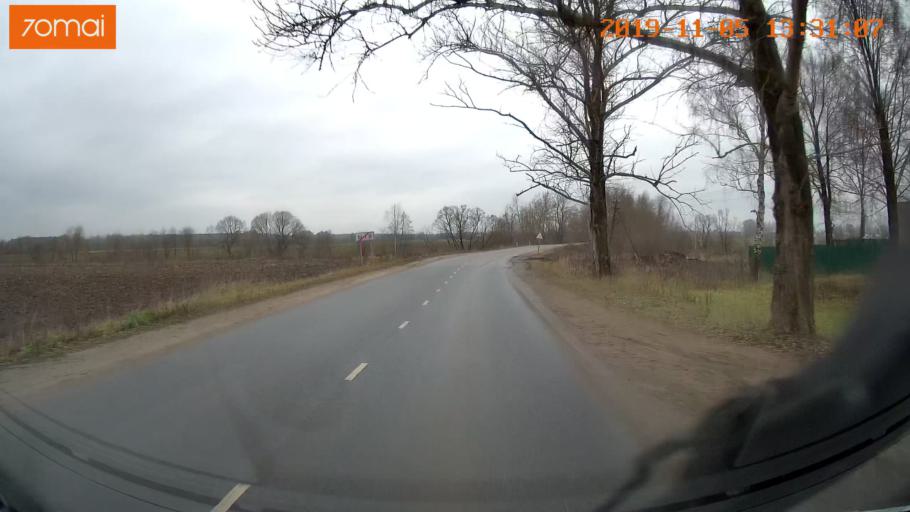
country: RU
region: Ivanovo
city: Shuya
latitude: 56.8724
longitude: 41.3925
